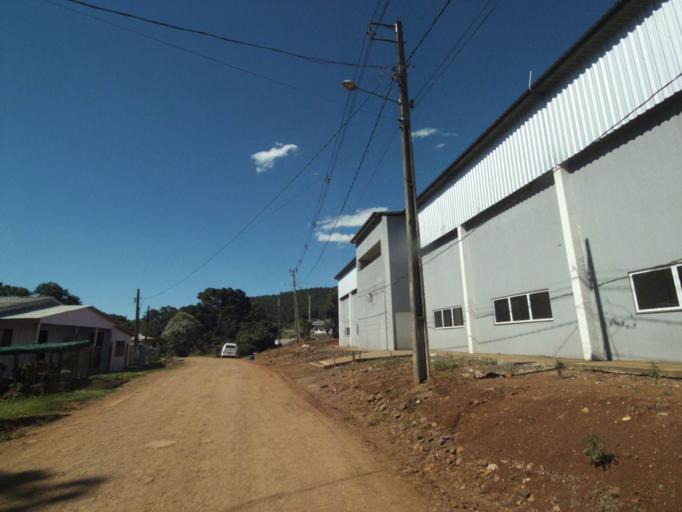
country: BR
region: Parana
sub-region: Ampere
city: Ampere
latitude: -26.1674
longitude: -53.3652
